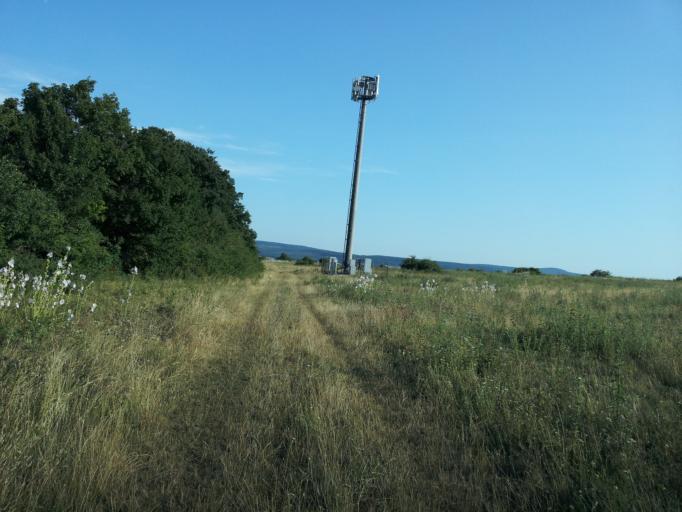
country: HU
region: Veszprem
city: Urkut
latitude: 47.0008
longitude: 17.6274
